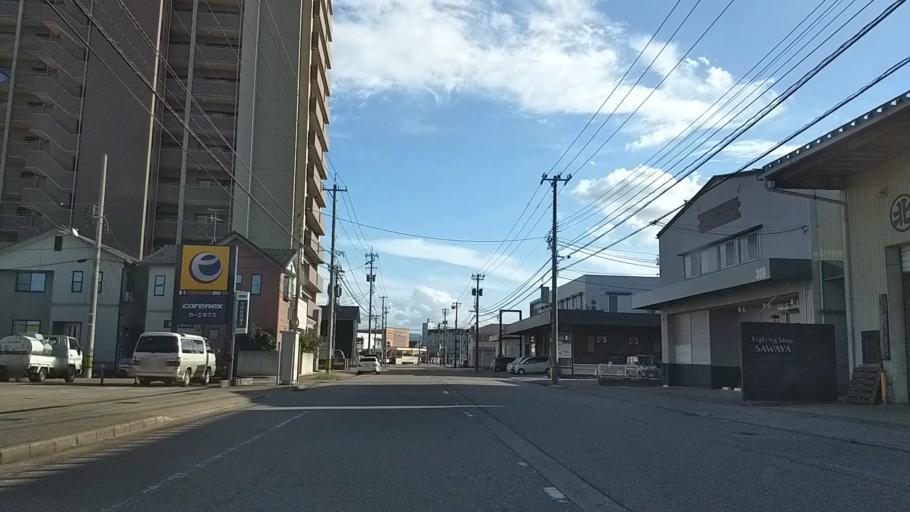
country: JP
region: Ishikawa
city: Kanazawa-shi
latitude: 36.5824
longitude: 136.6352
